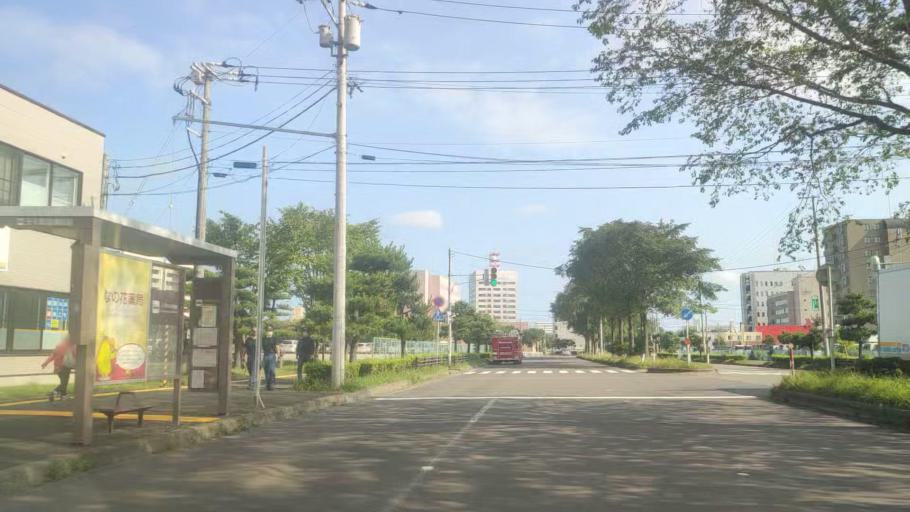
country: JP
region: Hokkaido
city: Tomakomai
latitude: 42.6377
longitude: 141.6027
